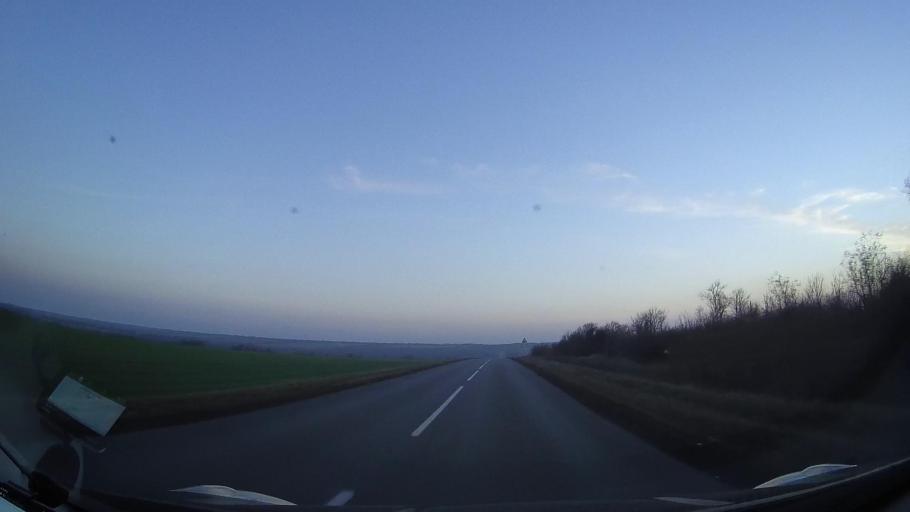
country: RU
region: Rostov
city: Zernograd
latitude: 46.9089
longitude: 40.3389
